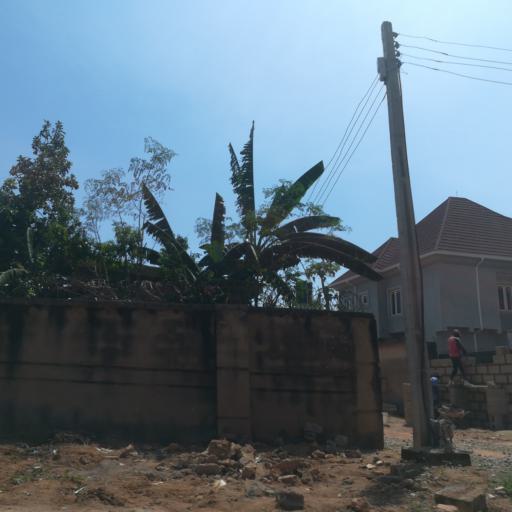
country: NG
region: Plateau
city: Bukuru
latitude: 9.8425
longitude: 8.9082
